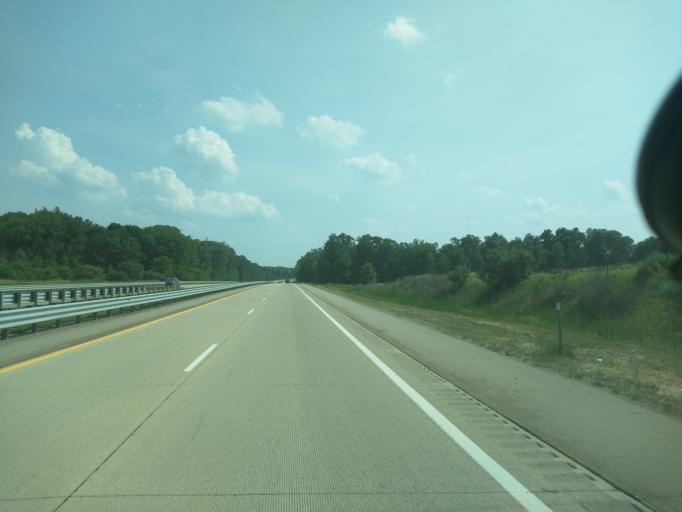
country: US
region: Michigan
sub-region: Jackson County
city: Jackson
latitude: 42.3274
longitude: -84.4290
